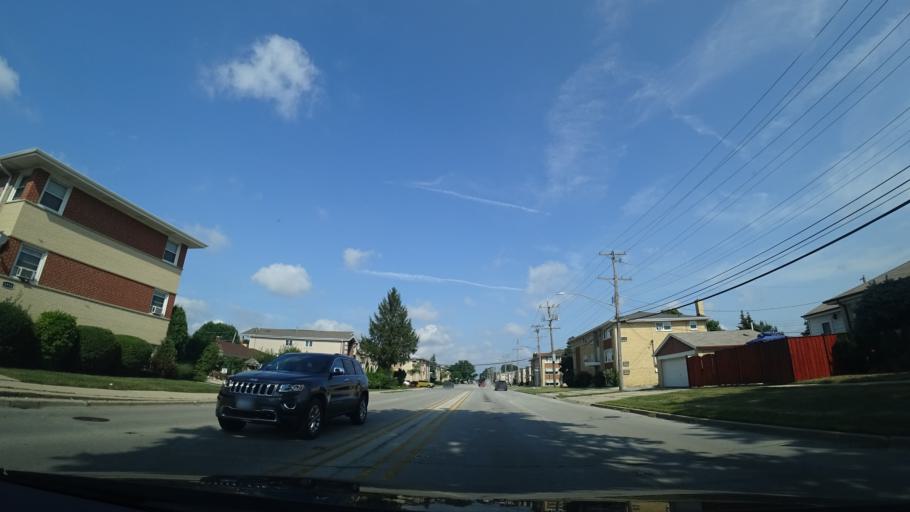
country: US
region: Illinois
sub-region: Cook County
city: Harwood Heights
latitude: 41.9683
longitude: -87.8025
